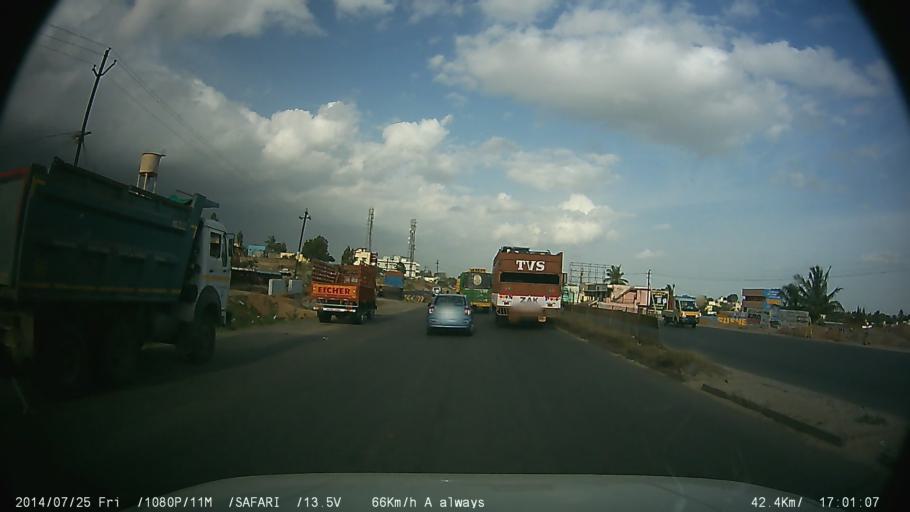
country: IN
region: Tamil Nadu
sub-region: Krishnagiri
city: Hosur
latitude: 12.7259
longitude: 77.8558
